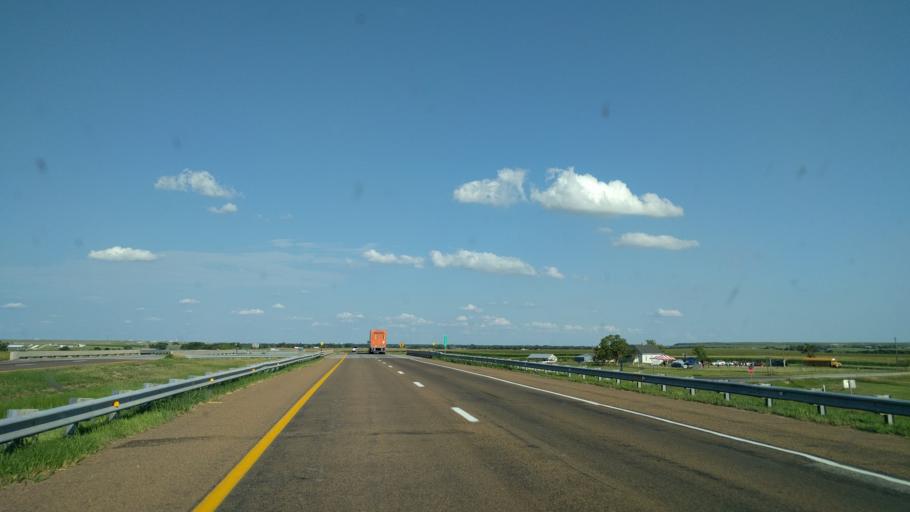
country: US
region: Kansas
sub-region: Ellis County
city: Hays
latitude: 38.9235
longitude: -99.4299
